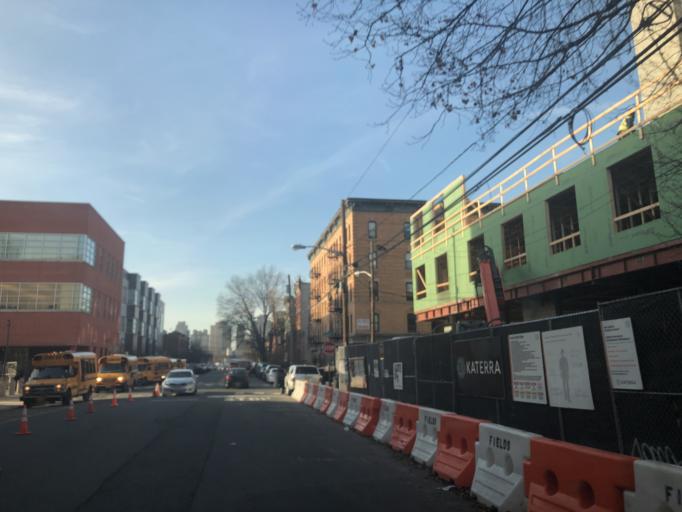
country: US
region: New Jersey
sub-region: Hudson County
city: Jersey City
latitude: 40.7177
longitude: -74.0495
